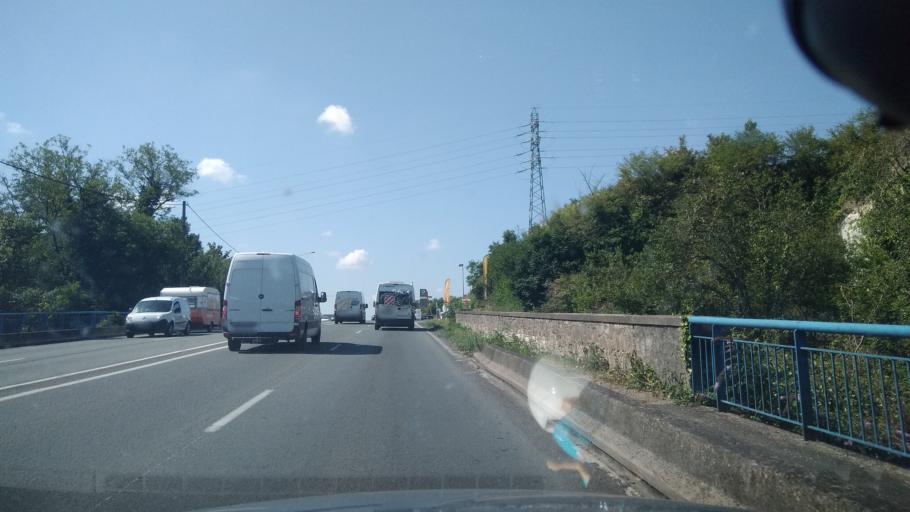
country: FR
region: Poitou-Charentes
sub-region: Departement de la Vienne
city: Chasseneuil-du-Poitou
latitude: 46.6330
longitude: 0.3573
